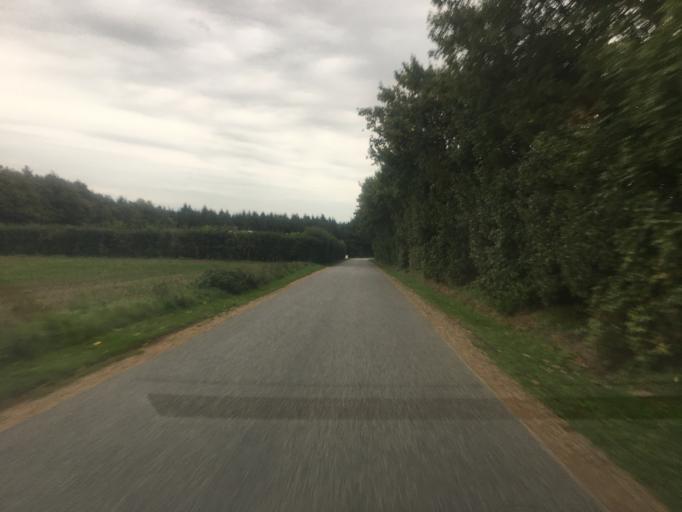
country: DK
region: South Denmark
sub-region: Tonder Kommune
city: Logumkloster
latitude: 55.0230
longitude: 9.0348
